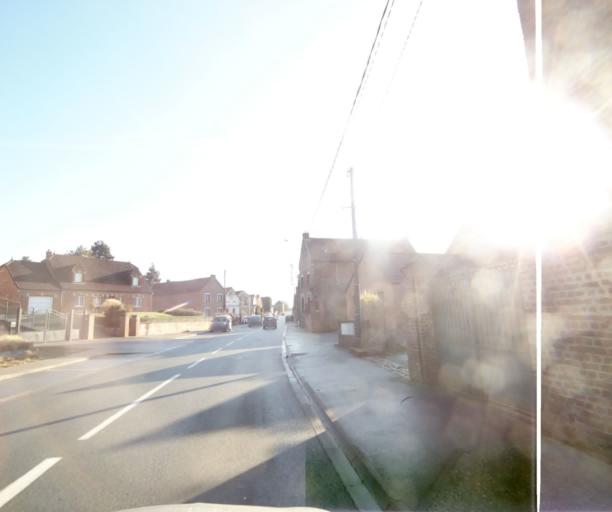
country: FR
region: Nord-Pas-de-Calais
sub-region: Departement du Nord
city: Preseau
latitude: 50.3109
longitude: 3.5782
